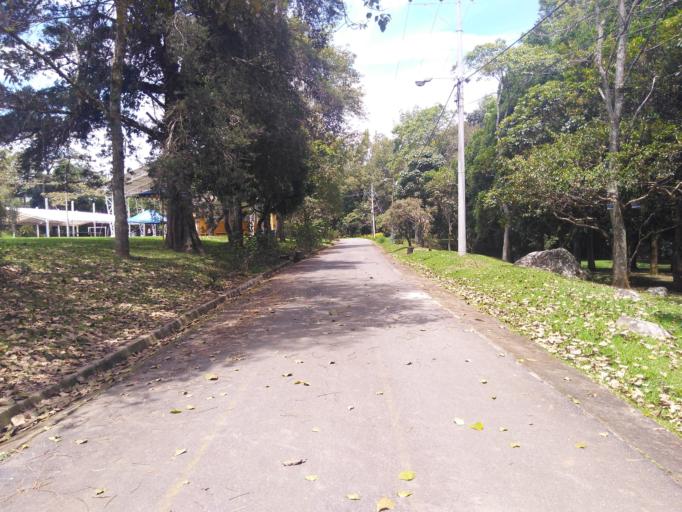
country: CO
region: Cauca
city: Popayan
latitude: 2.4777
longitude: -76.5716
